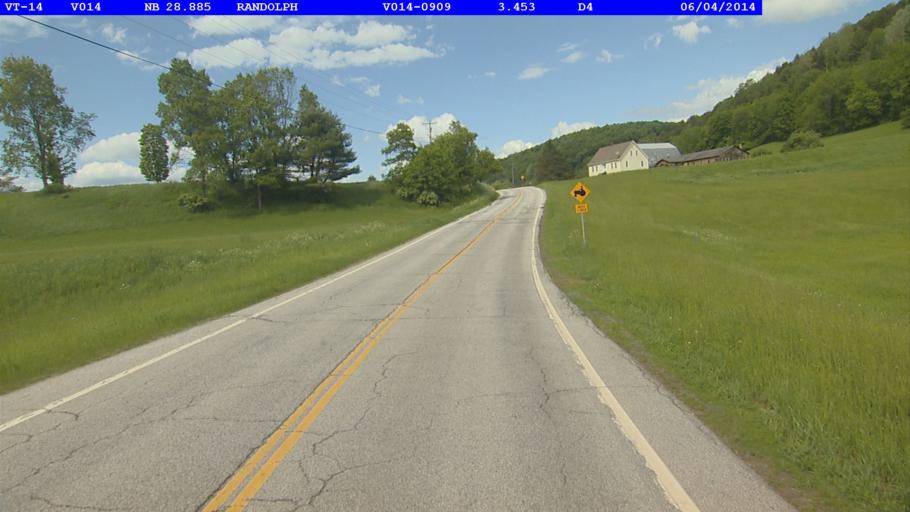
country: US
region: Vermont
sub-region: Orange County
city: Randolph
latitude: 43.9194
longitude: -72.5551
